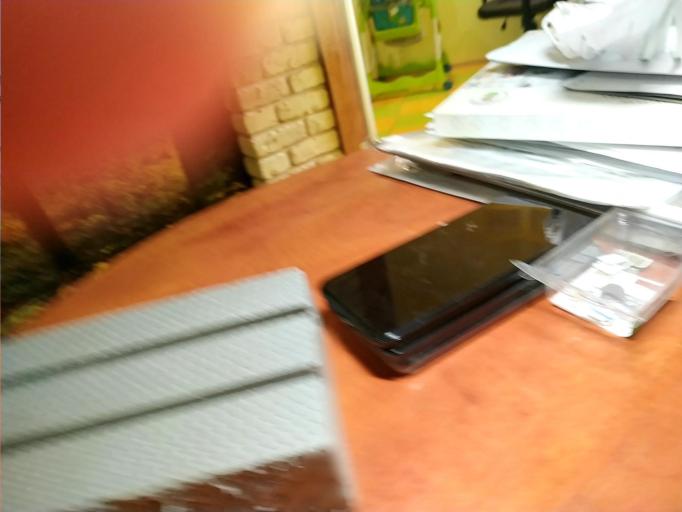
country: RU
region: Smolensk
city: Katyn'
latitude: 54.8604
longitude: 31.6764
